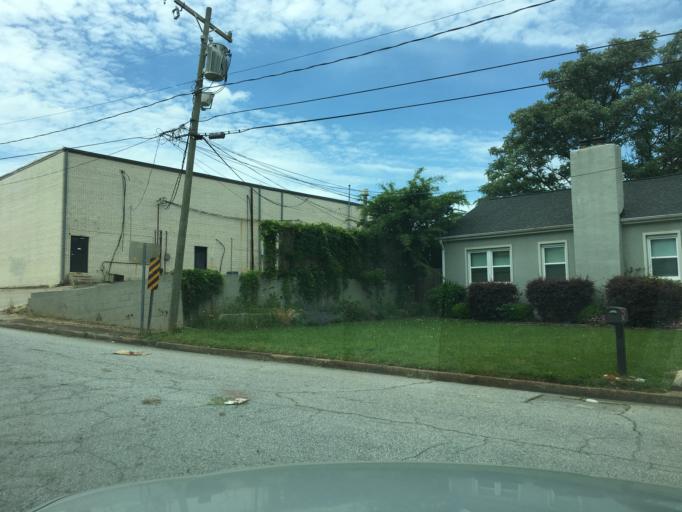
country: US
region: South Carolina
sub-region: Greenville County
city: Greenville
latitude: 34.8446
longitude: -82.3631
